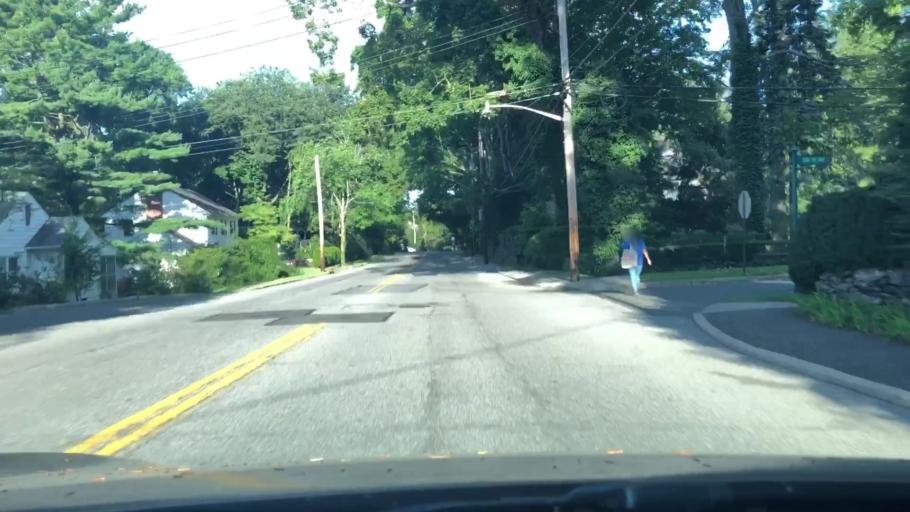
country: US
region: New York
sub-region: Westchester County
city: Bronxville
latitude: 40.9343
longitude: -73.8273
